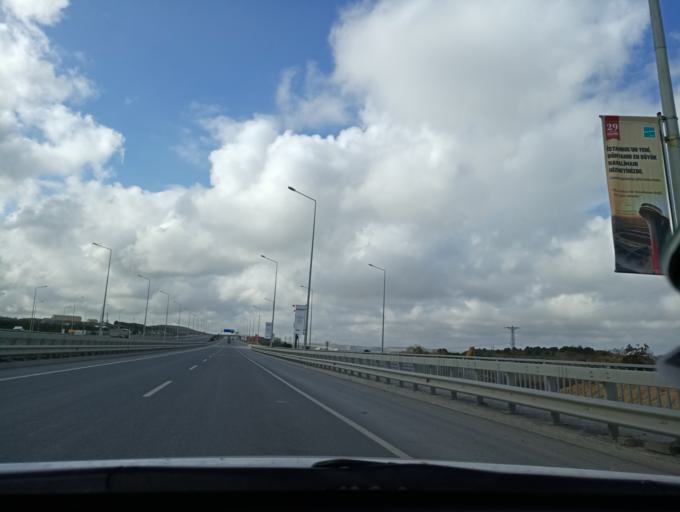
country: TR
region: Istanbul
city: Durusu
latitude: 41.2453
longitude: 28.7667
